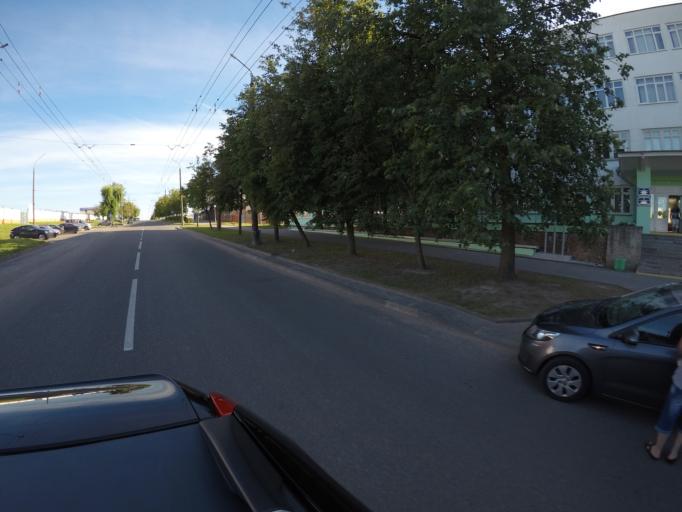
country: BY
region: Grodnenskaya
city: Hrodna
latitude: 53.7120
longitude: 23.8263
